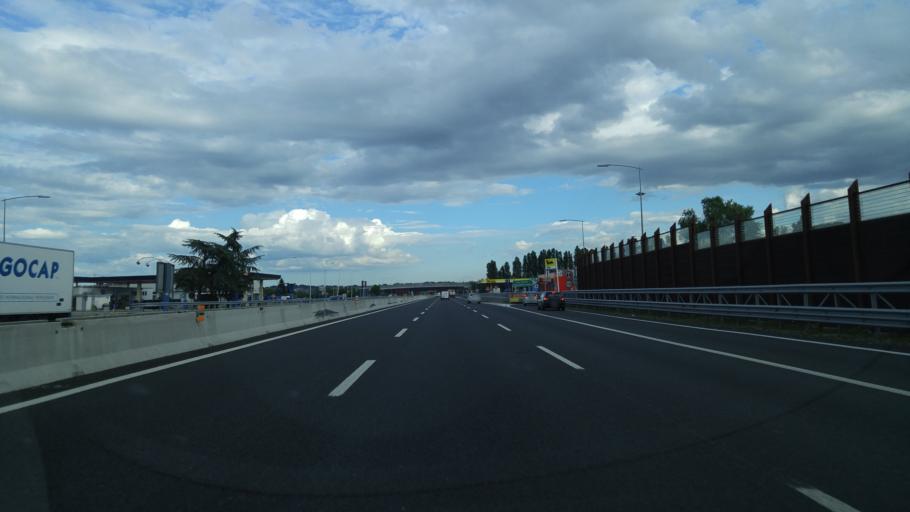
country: IT
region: Emilia-Romagna
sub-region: Provincia di Rimini
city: Coriano
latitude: 43.9958
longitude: 12.6168
